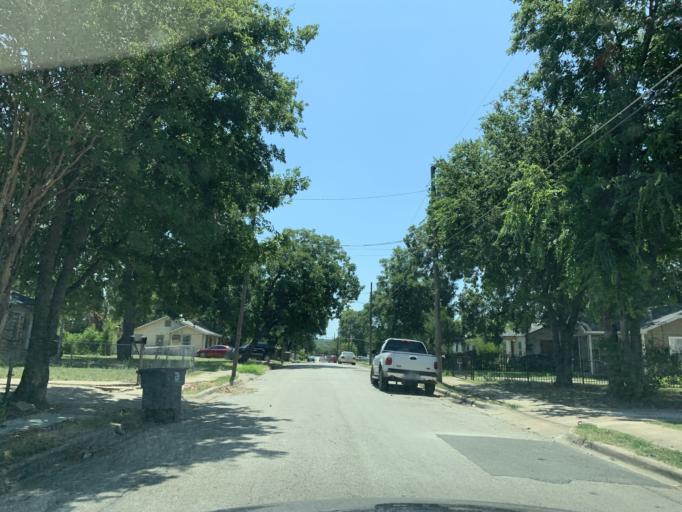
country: US
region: Texas
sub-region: Dallas County
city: Hutchins
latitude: 32.6896
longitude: -96.7925
